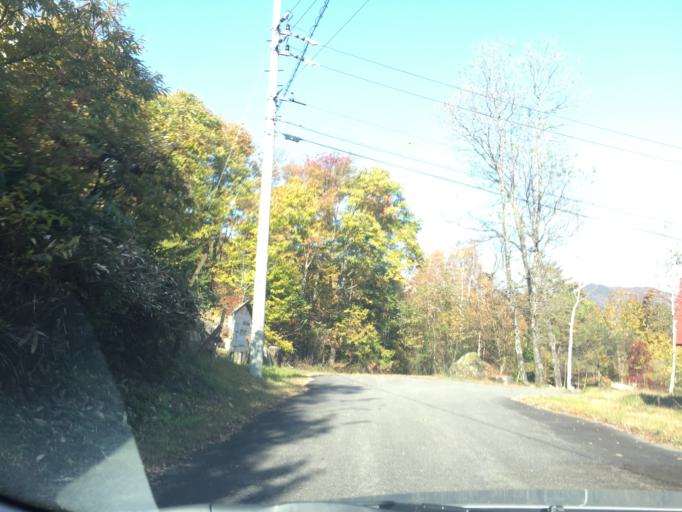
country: JP
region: Gifu
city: Nakatsugawa
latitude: 35.3693
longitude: 137.6740
